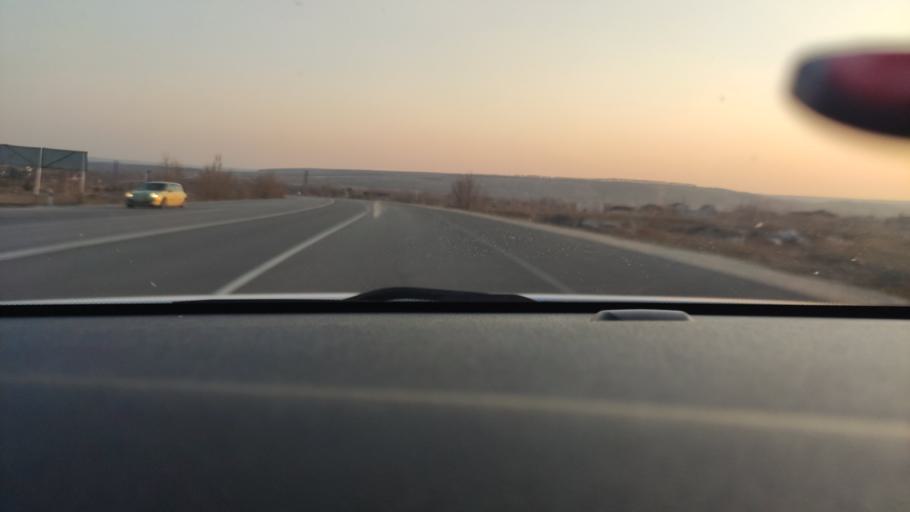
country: RU
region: Voronezj
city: Kolodeznyy
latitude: 51.3551
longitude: 39.1758
